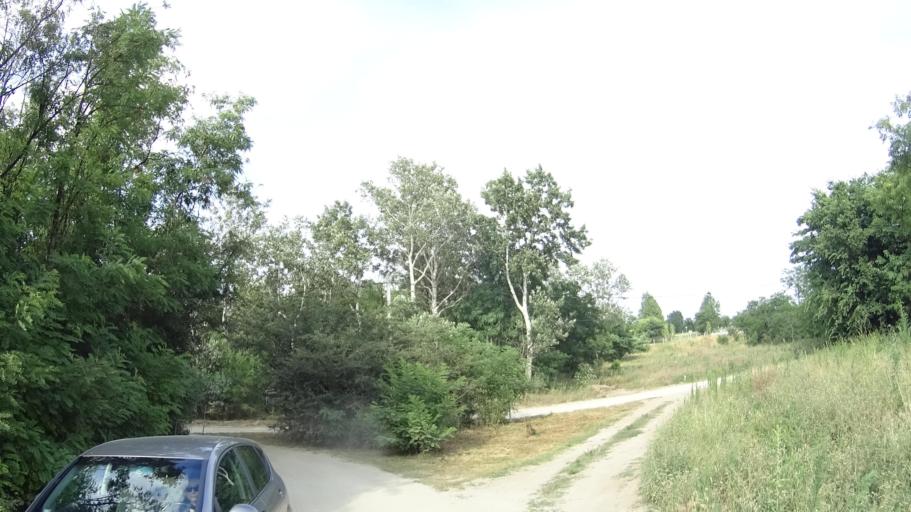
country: HU
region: Pest
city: Dunavarsany
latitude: 47.2986
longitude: 19.0358
